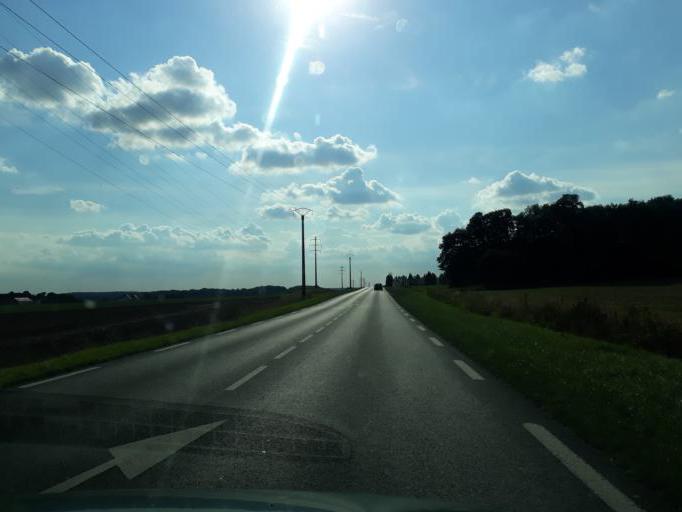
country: FR
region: Centre
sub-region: Departement du Loir-et-Cher
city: Moree
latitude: 47.9043
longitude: 1.2810
